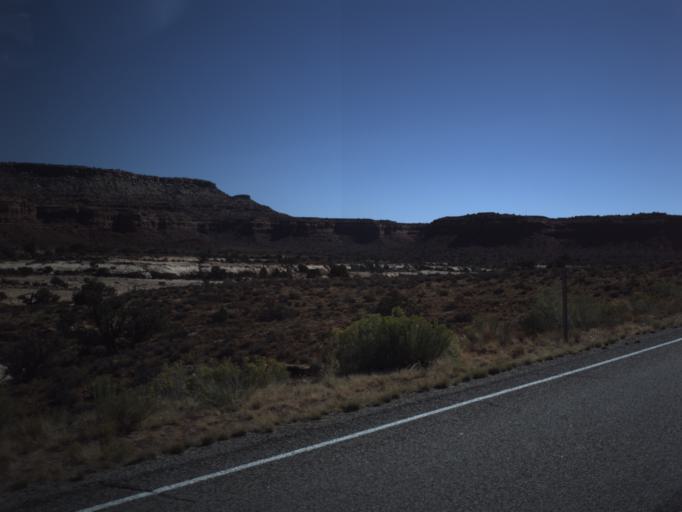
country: US
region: Utah
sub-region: San Juan County
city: Blanding
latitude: 37.7221
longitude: -110.2482
